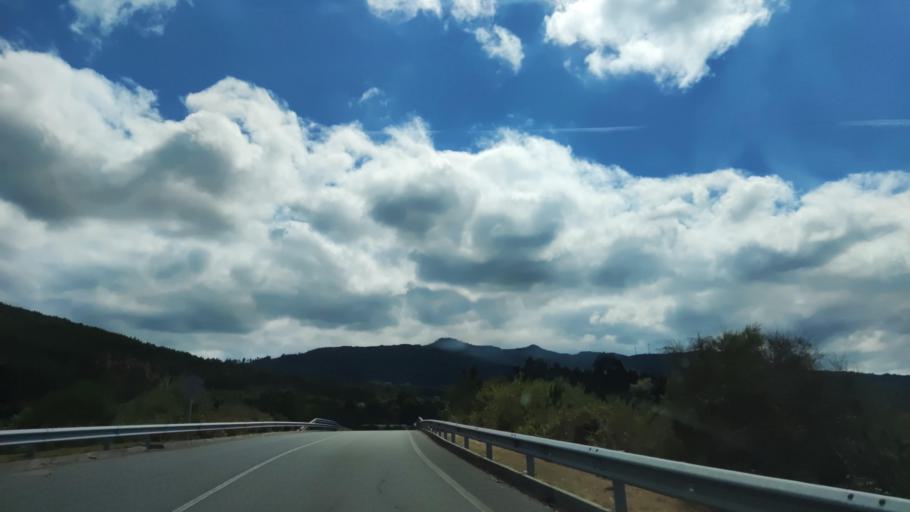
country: ES
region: Galicia
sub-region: Provincia da Coruna
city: Padron
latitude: 42.7834
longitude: -8.6566
